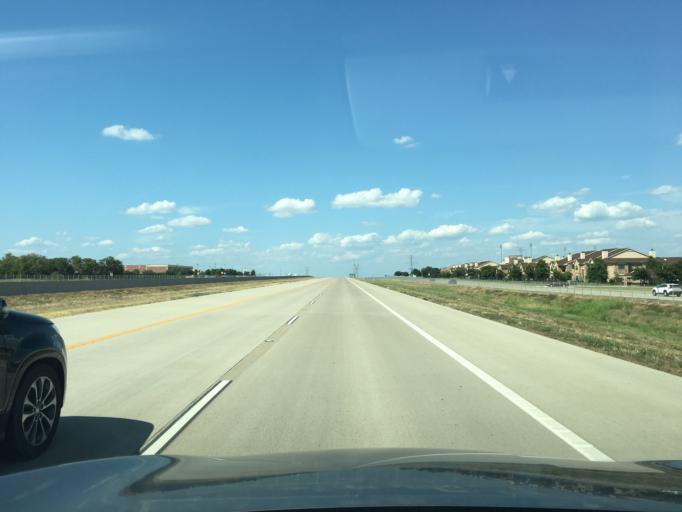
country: US
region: Texas
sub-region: Tarrant County
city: Mansfield
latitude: 32.5690
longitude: -97.0827
